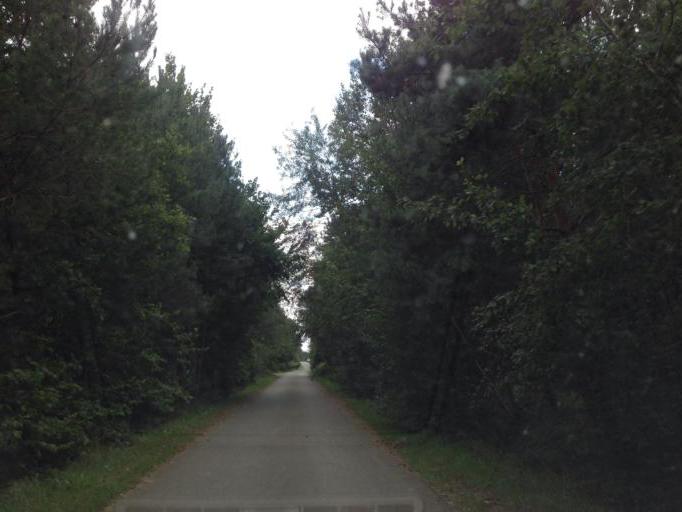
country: DE
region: Lower Saxony
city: Adendorf
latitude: 53.2965
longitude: 10.4393
